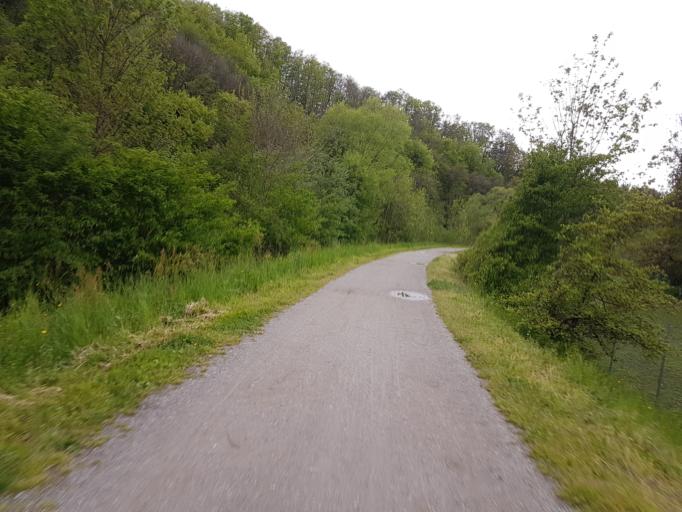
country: DE
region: Baden-Wuerttemberg
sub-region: Freiburg Region
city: Lauchringen
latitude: 47.6235
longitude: 8.3014
